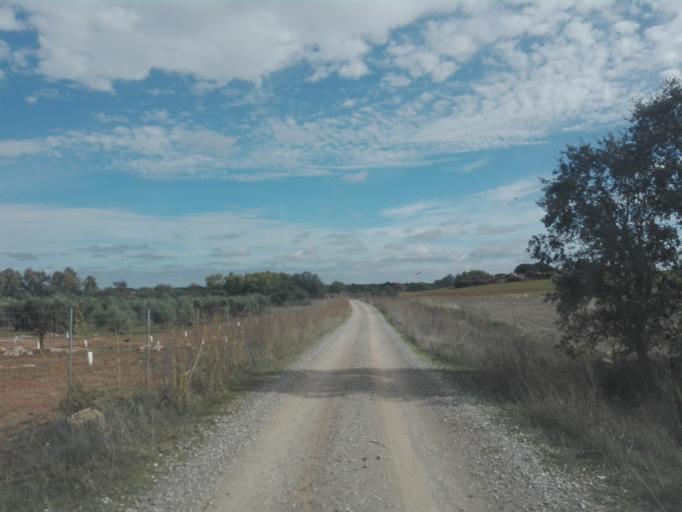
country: ES
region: Extremadura
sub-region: Provincia de Badajoz
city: Villagarcia de la Torre
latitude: 38.2924
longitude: -6.0993
